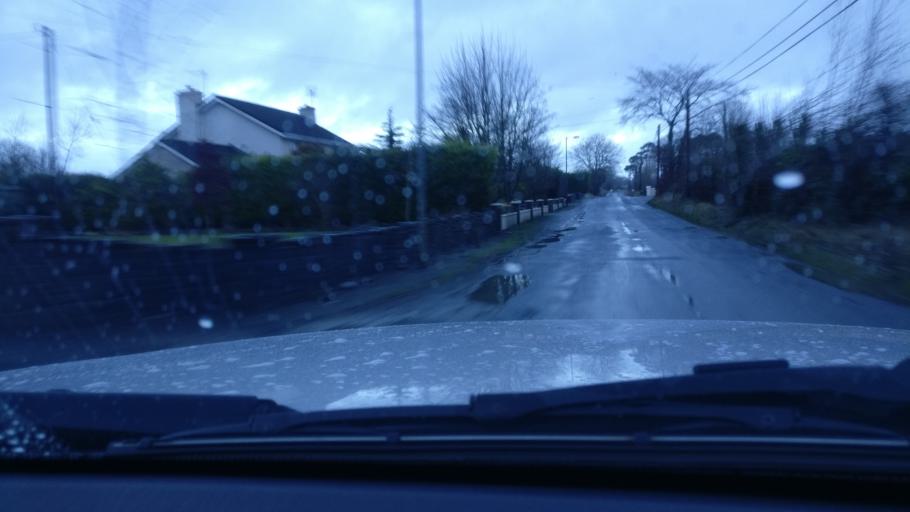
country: IE
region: Connaught
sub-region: County Galway
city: Ballinasloe
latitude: 53.2433
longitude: -8.2678
